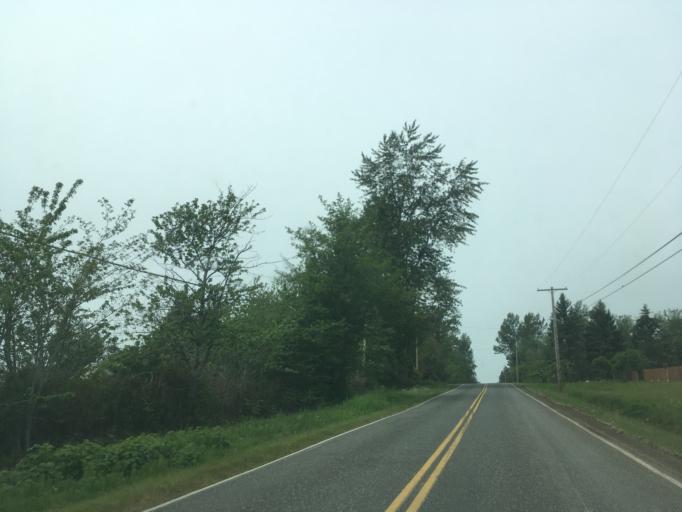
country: US
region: Washington
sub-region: Whatcom County
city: Bellingham
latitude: 48.8188
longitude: -122.4648
